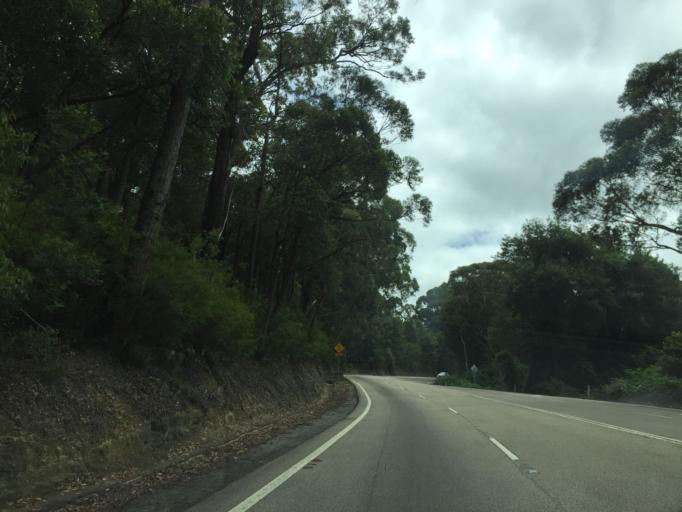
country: AU
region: New South Wales
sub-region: Hawkesbury
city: Richmond
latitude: -33.5405
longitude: 150.6331
